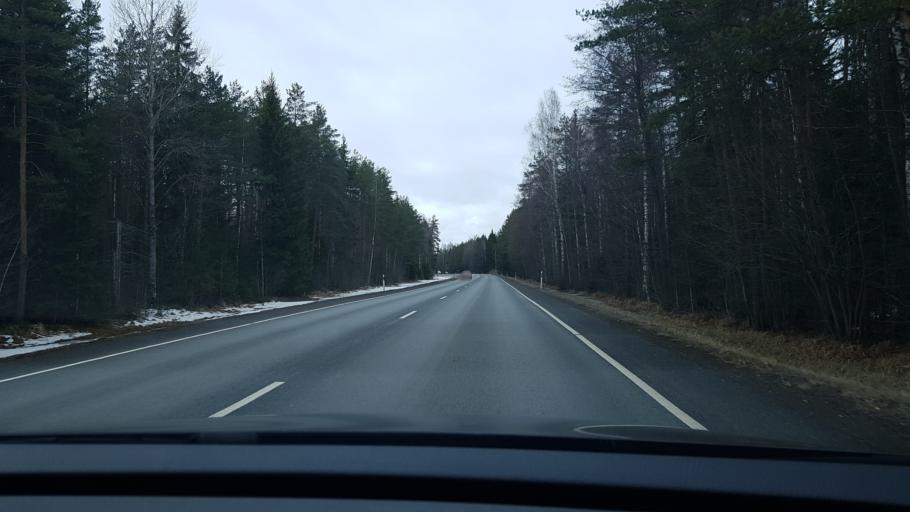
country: EE
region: Paernumaa
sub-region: Paikuse vald
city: Paikuse
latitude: 58.2484
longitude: 24.6868
